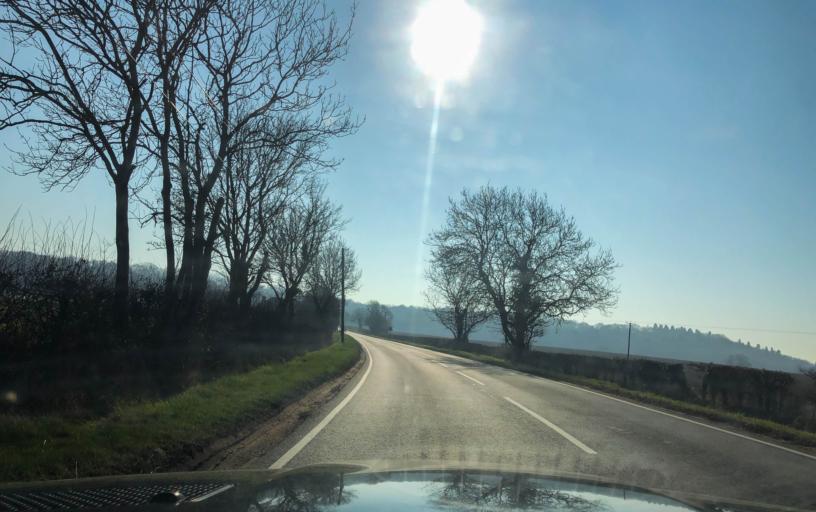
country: GB
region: England
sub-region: Warwickshire
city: Wellesbourne Mountford
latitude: 52.1859
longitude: -1.5790
